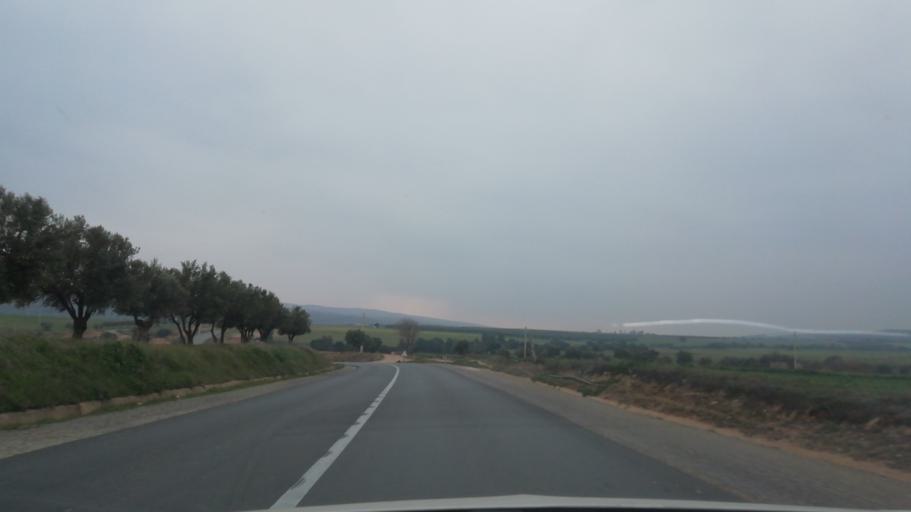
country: DZ
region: Sidi Bel Abbes
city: Sfizef
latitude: 35.2769
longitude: -0.1544
